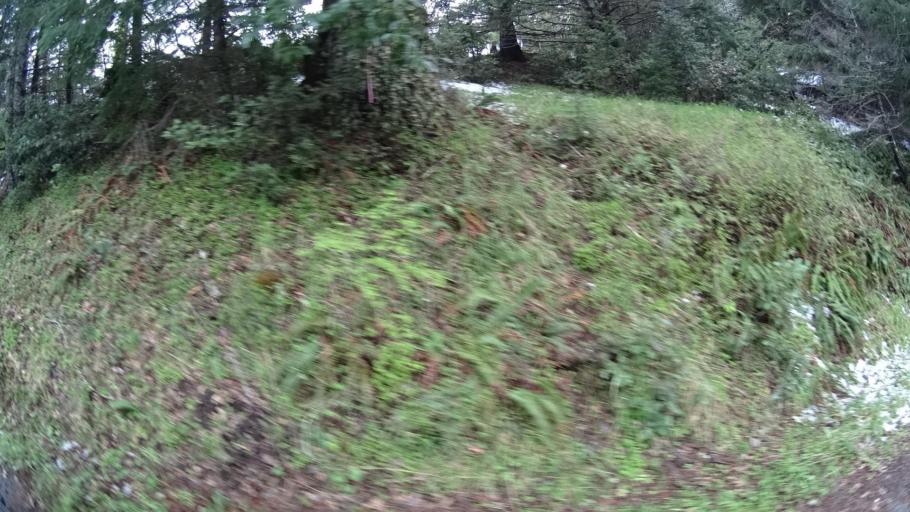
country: US
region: California
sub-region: Humboldt County
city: Blue Lake
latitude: 40.8807
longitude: -123.8722
